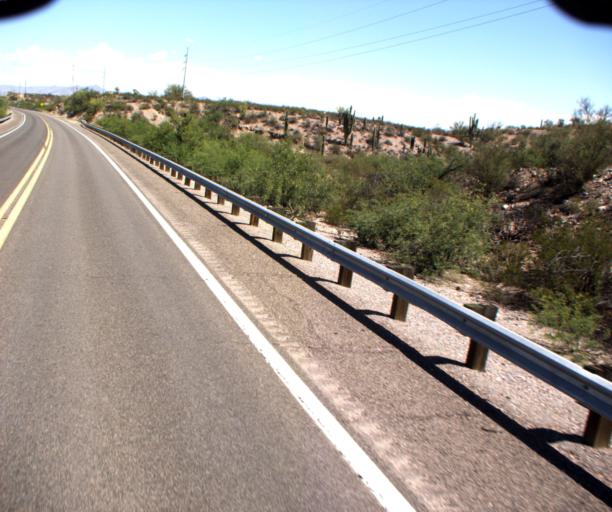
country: US
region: Arizona
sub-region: Pinal County
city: Mammoth
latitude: 32.9131
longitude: -110.7194
